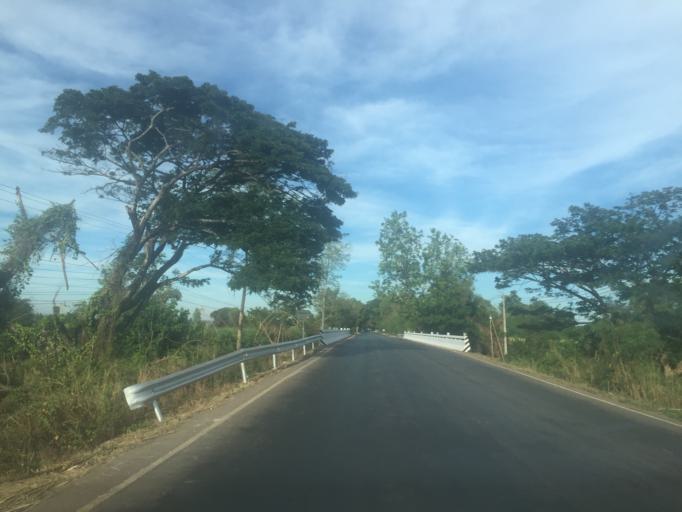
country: TH
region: Kalasin
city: Tha Khantho
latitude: 16.9624
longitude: 103.2535
